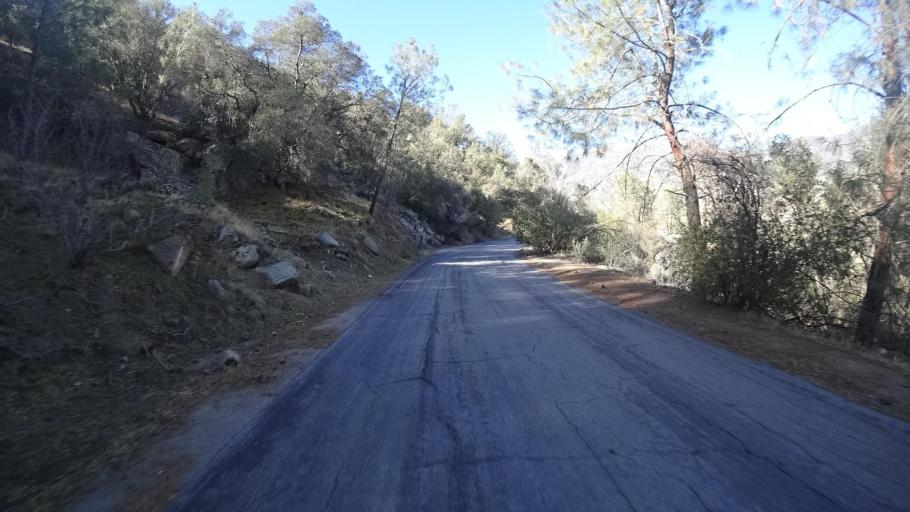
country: US
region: California
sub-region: Kern County
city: Bodfish
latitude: 35.5516
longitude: -118.6025
